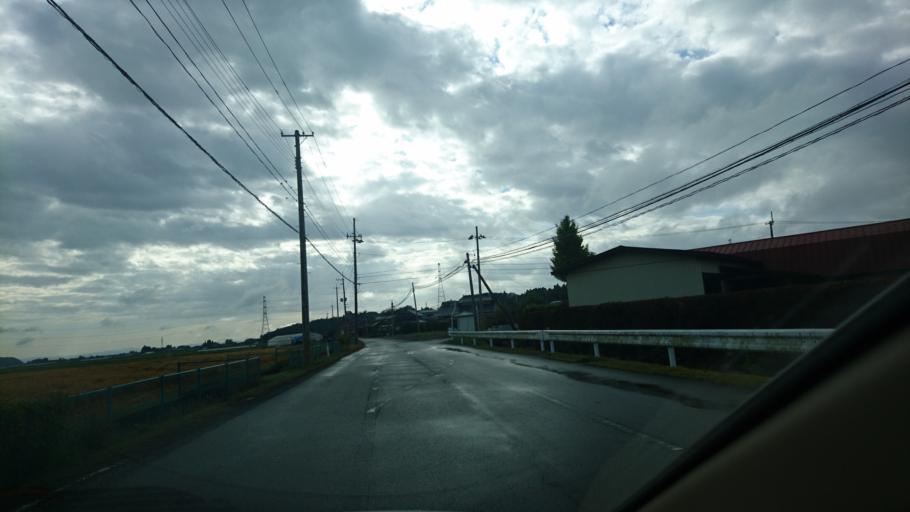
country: JP
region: Iwate
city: Ichinoseki
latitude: 38.7995
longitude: 140.9906
